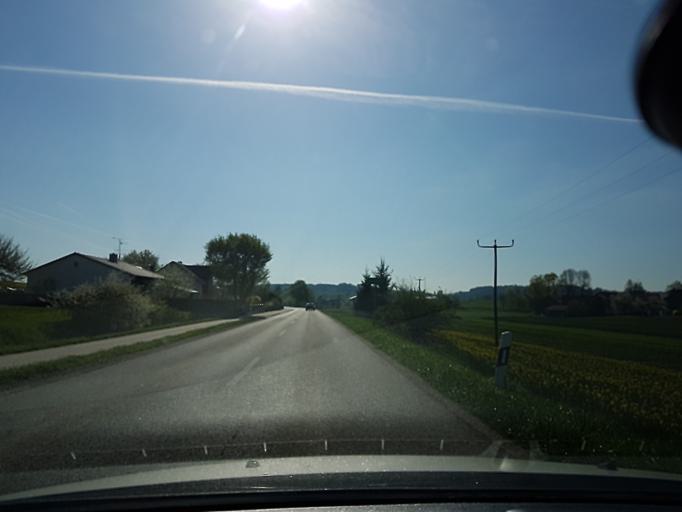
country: DE
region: Bavaria
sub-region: Lower Bavaria
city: Furth
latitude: 48.4049
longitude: 12.3833
